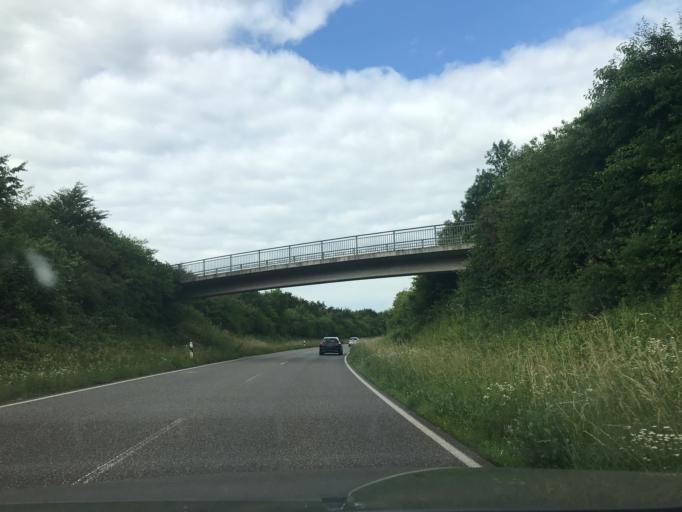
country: DE
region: North Rhine-Westphalia
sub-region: Regierungsbezirk Dusseldorf
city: Neuss
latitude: 51.1574
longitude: 6.7169
